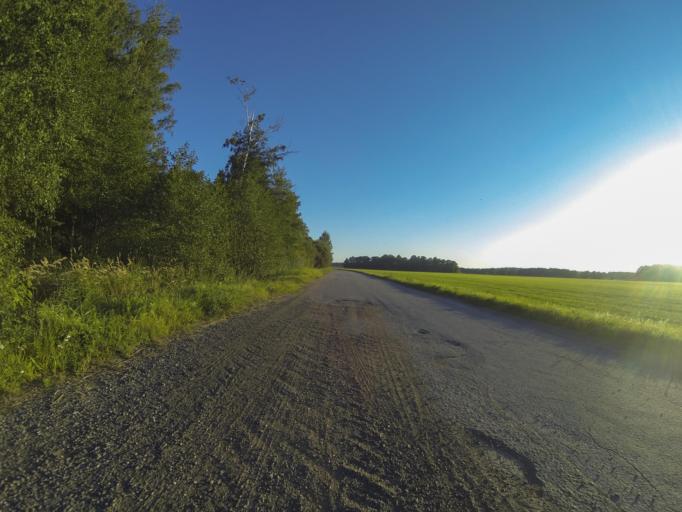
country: SE
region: Vaestmanland
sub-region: Vasteras
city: Vasteras
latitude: 59.5773
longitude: 16.6562
